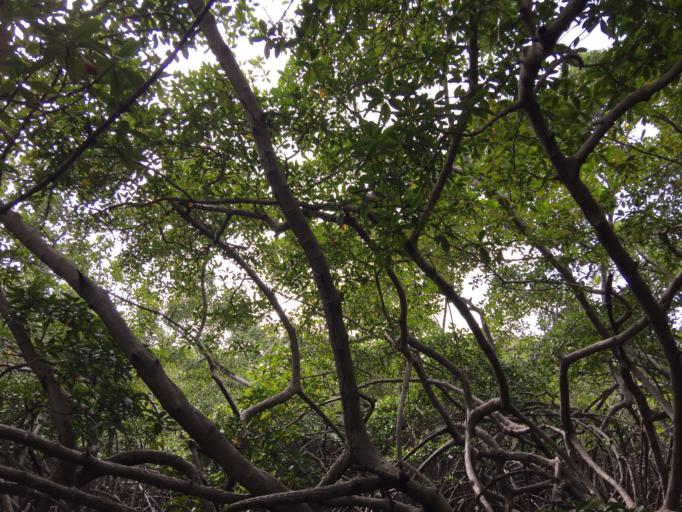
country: SN
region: Fatick
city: Sokone
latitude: 13.8125
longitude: -16.4943
